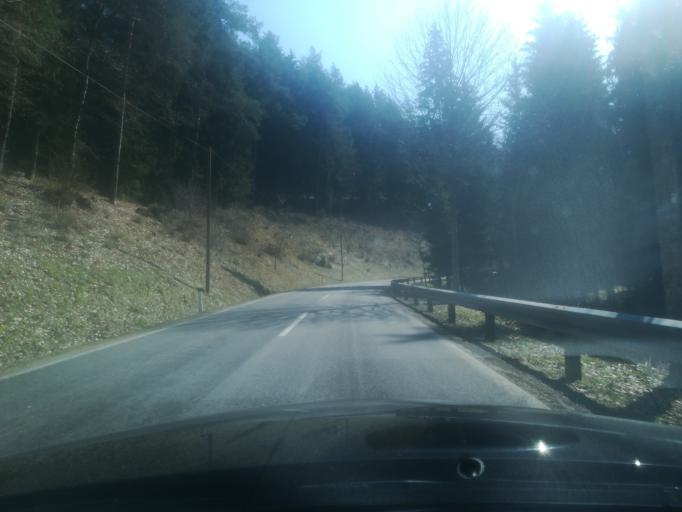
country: AT
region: Upper Austria
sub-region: Politischer Bezirk Freistadt
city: Freistadt
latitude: 48.4362
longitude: 14.5628
